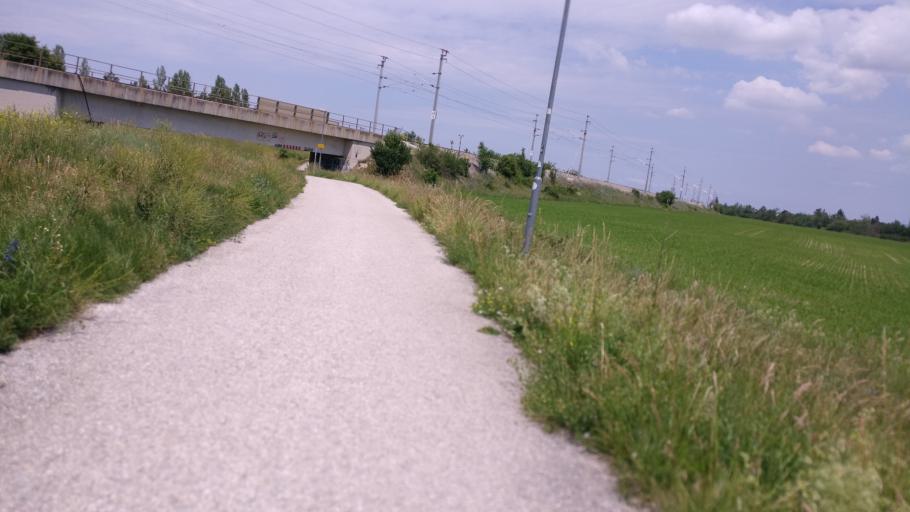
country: AT
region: Lower Austria
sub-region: Politischer Bezirk Wiener Neustadt
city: Lichtenworth
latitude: 47.8363
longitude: 16.2677
